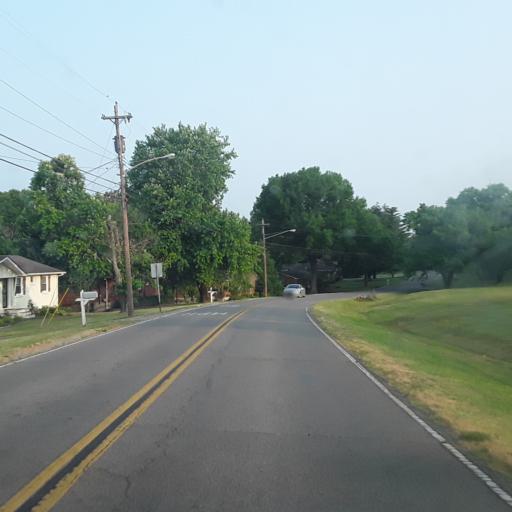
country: US
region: Tennessee
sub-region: Williamson County
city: Brentwood
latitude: 36.0571
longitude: -86.7267
